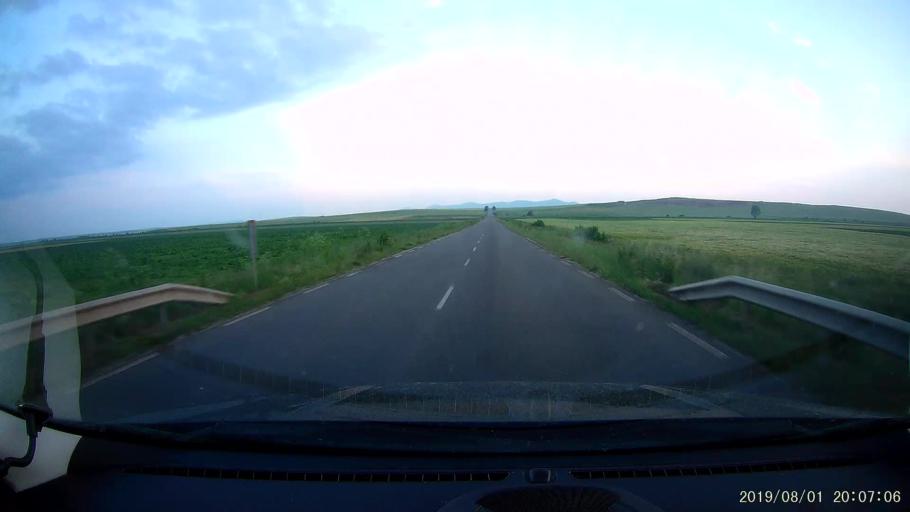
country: BG
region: Yambol
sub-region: Obshtina Yambol
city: Yambol
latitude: 42.5270
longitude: 26.5629
